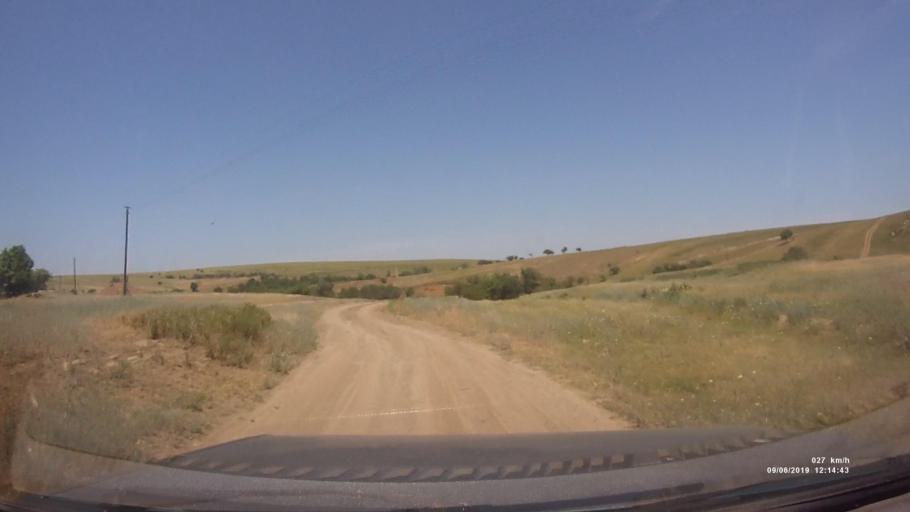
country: RU
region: Rostov
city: Staraya Stanitsa
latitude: 48.2527
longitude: 40.3233
